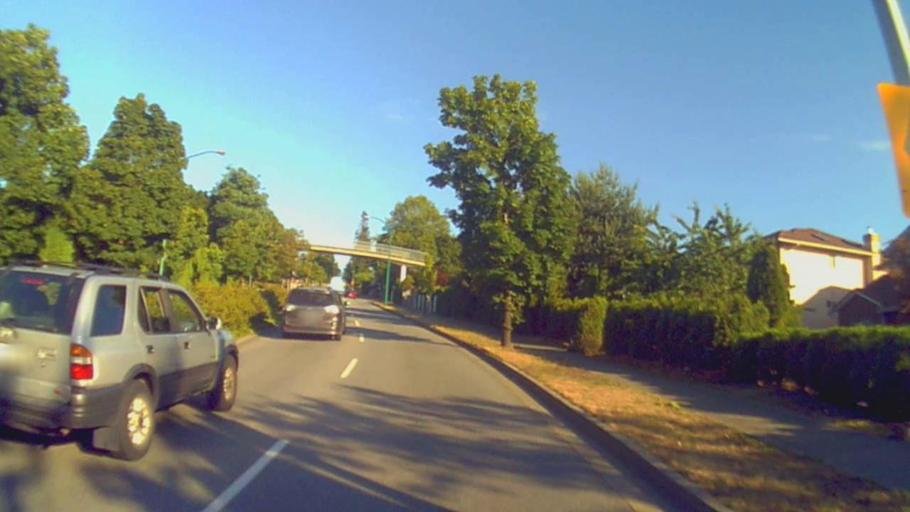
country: CA
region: British Columbia
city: New Westminster
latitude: 49.2368
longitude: -122.9063
